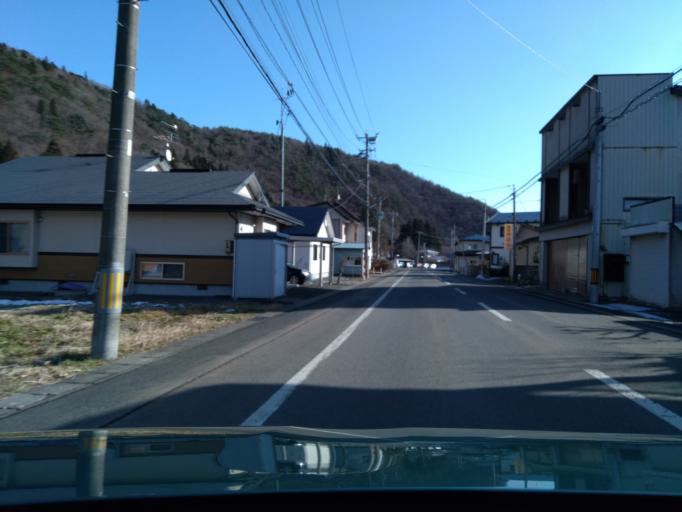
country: JP
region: Iwate
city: Hanamaki
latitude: 39.4366
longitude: 141.0140
